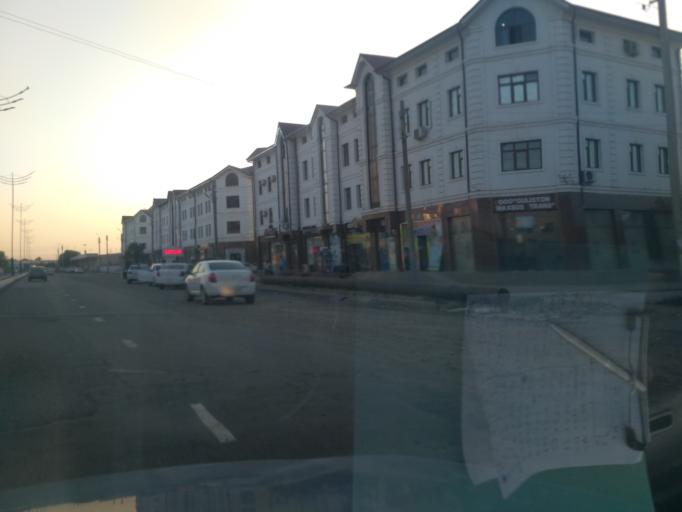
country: UZ
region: Sirdaryo
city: Guliston
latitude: 40.4983
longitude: 68.7687
